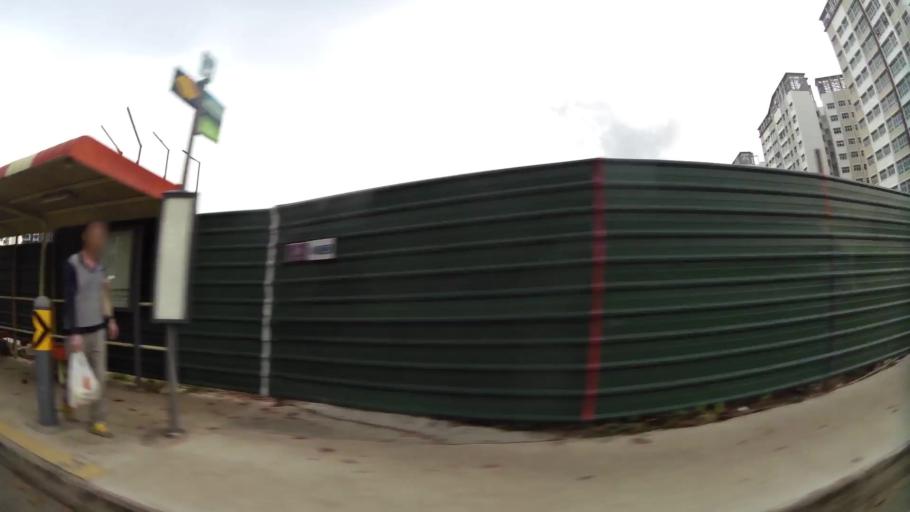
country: MY
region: Johor
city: Kampung Pasir Gudang Baru
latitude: 1.4175
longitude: 103.8421
